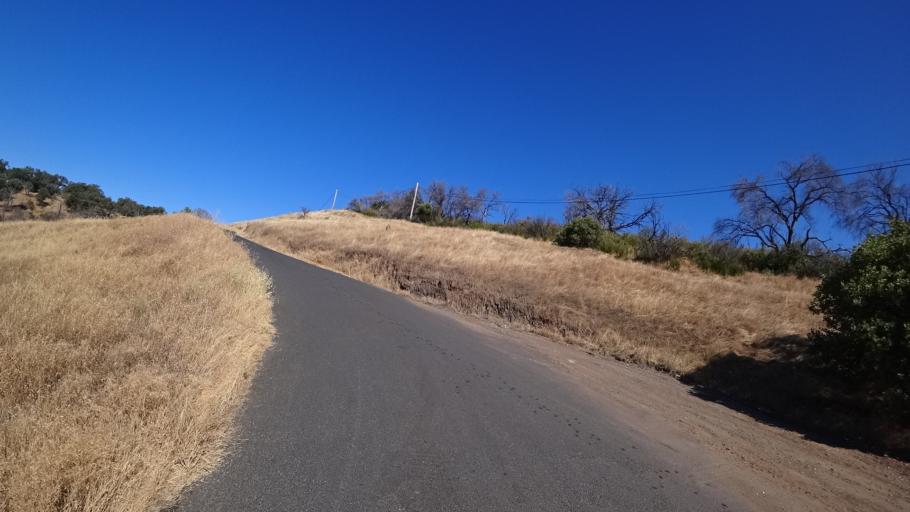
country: US
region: California
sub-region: Calaveras County
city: San Andreas
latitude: 38.2312
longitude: -120.6581
